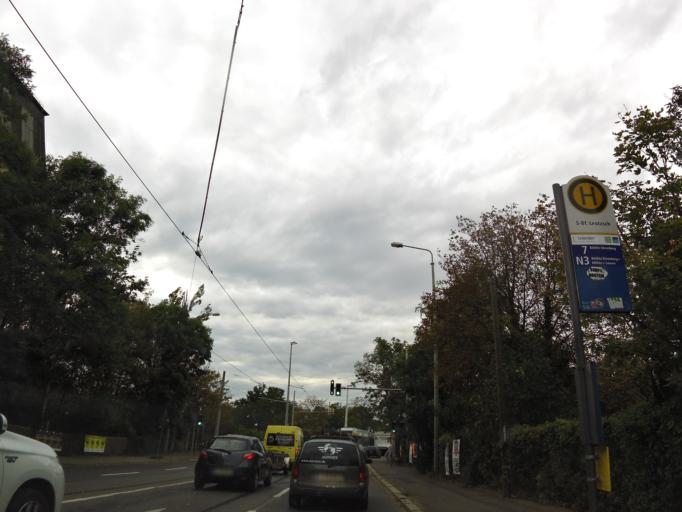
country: DE
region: Saxony
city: Leipzig
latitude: 51.3528
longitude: 12.3037
